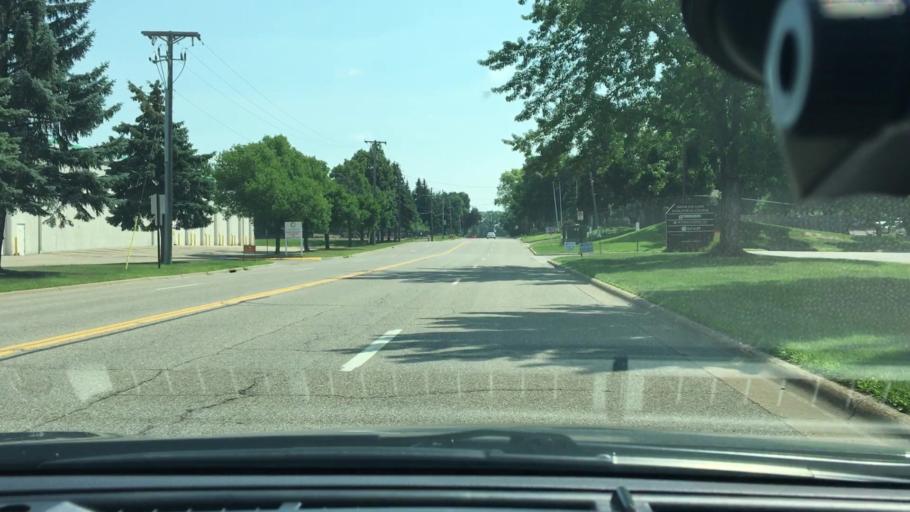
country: US
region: Minnesota
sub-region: Hennepin County
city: Plymouth
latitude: 44.9894
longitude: -93.4075
